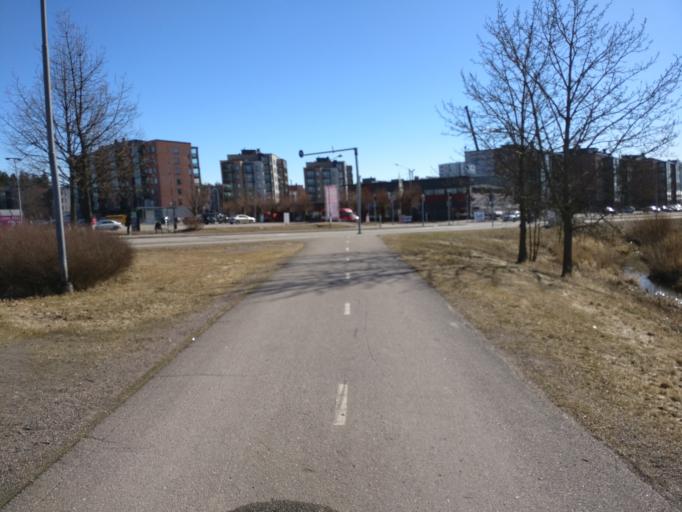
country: FI
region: Uusimaa
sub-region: Helsinki
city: Jaervenpaeae
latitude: 60.4790
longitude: 25.0841
